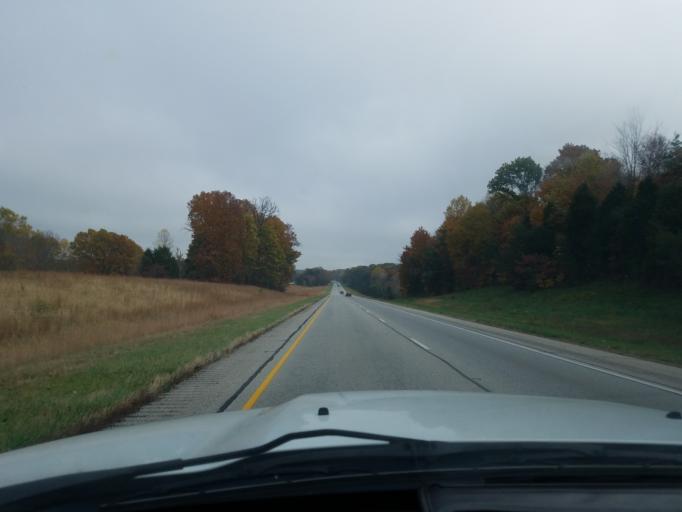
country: US
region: Indiana
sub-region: Floyd County
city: Georgetown
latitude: 38.2526
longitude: -86.0391
